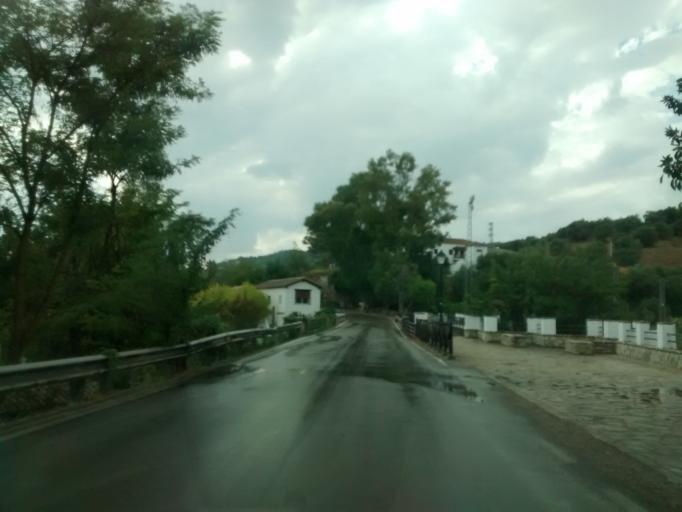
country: ES
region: Andalusia
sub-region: Provincia de Cadiz
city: El Bosque
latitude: 36.7581
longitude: -5.5083
